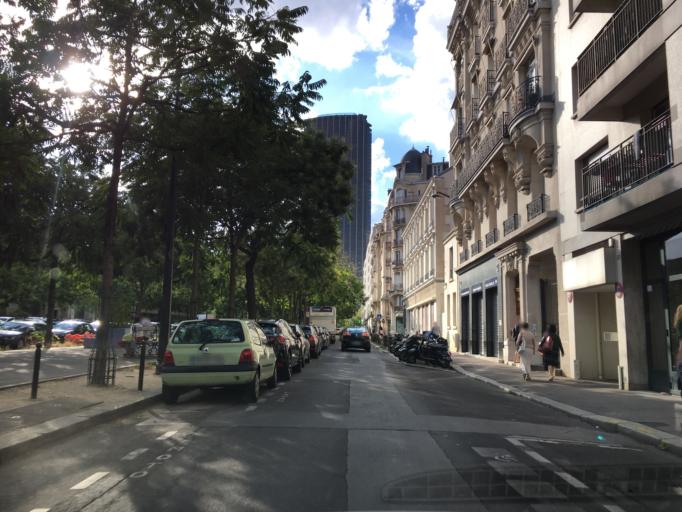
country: FR
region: Ile-de-France
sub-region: Paris
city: Paris
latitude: 48.8400
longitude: 2.3289
